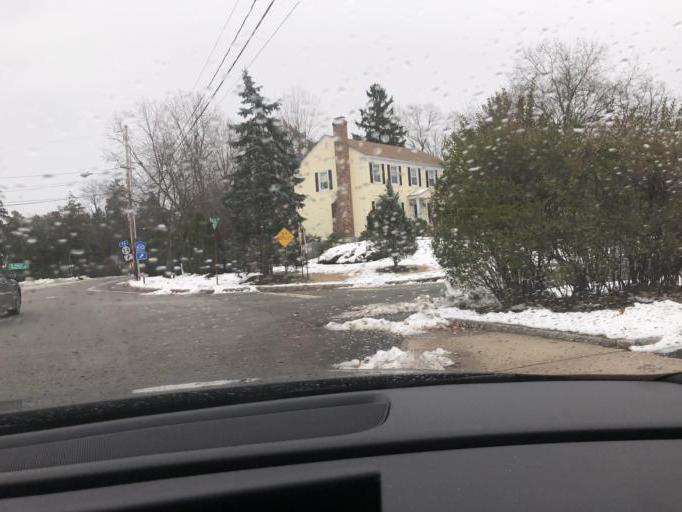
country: US
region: New Jersey
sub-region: Morris County
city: Morristown
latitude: 40.7964
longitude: -74.4598
